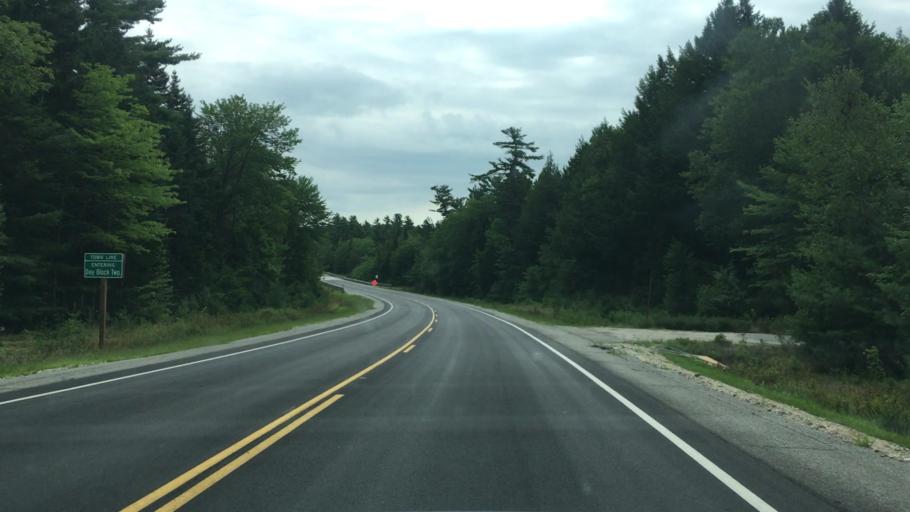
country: US
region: Maine
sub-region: Washington County
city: Addison
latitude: 44.9083
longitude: -67.8433
